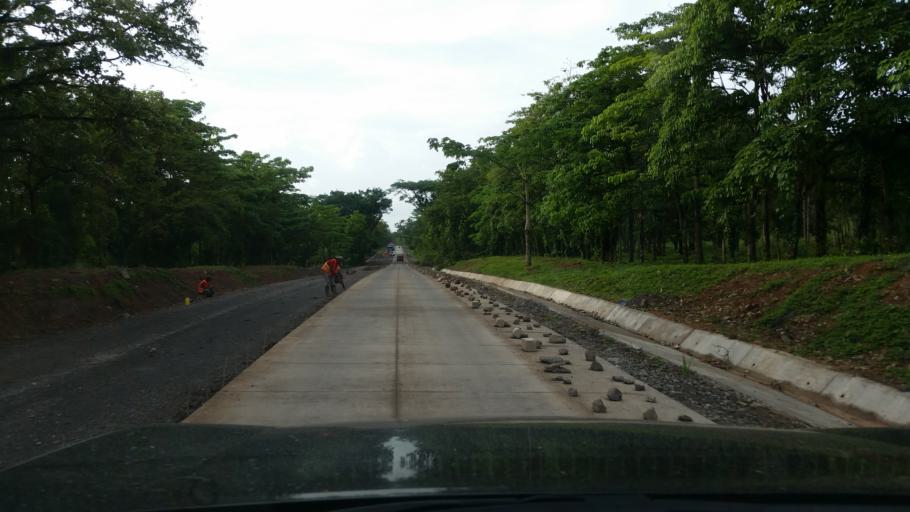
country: NI
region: Matagalpa
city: Rio Blanco
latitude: 13.0861
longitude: -85.0621
